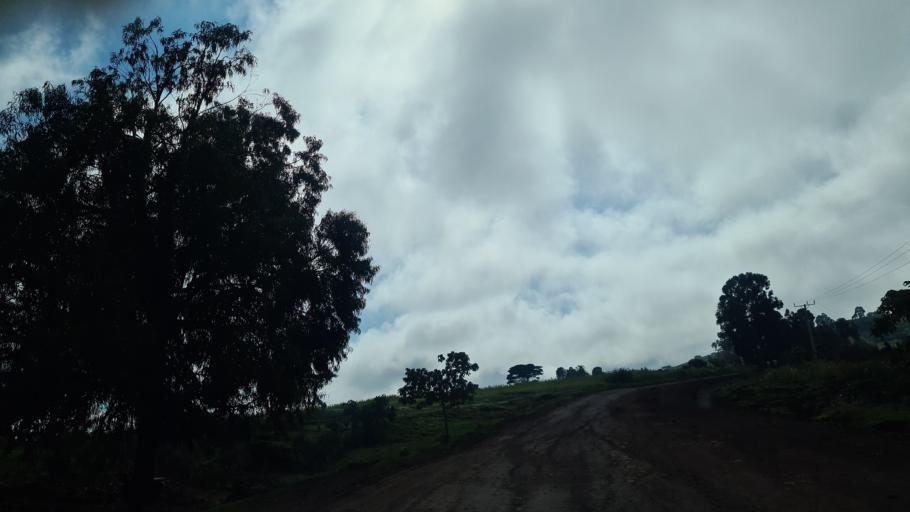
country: ET
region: Oromiya
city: Huruta
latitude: 8.1306
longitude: 39.3856
